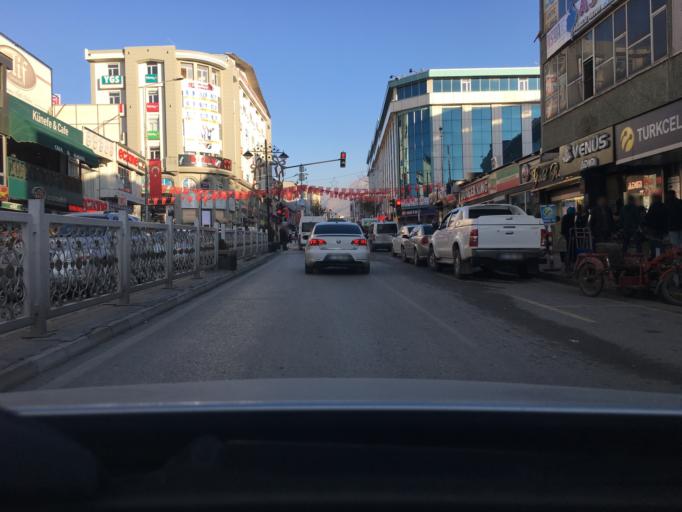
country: TR
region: Van
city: Van
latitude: 38.4988
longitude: 43.3933
